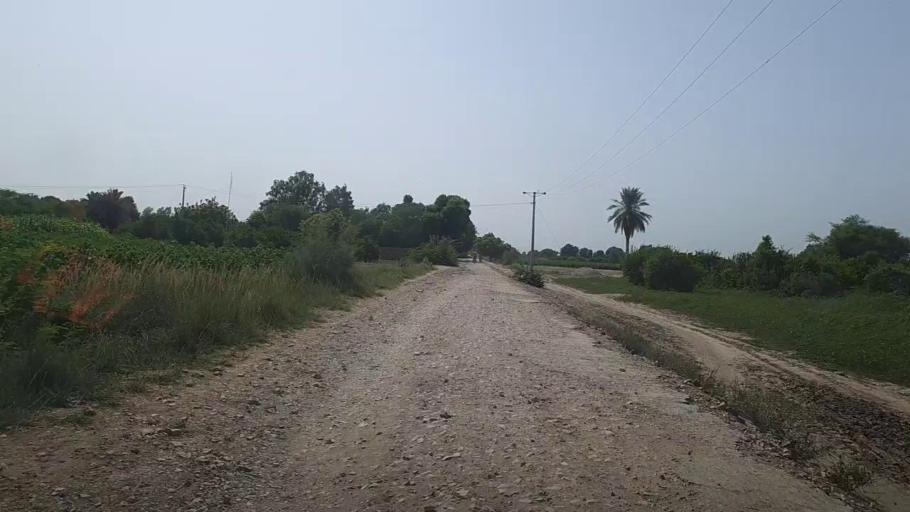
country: PK
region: Sindh
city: Pad Idan
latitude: 26.7631
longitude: 68.3326
